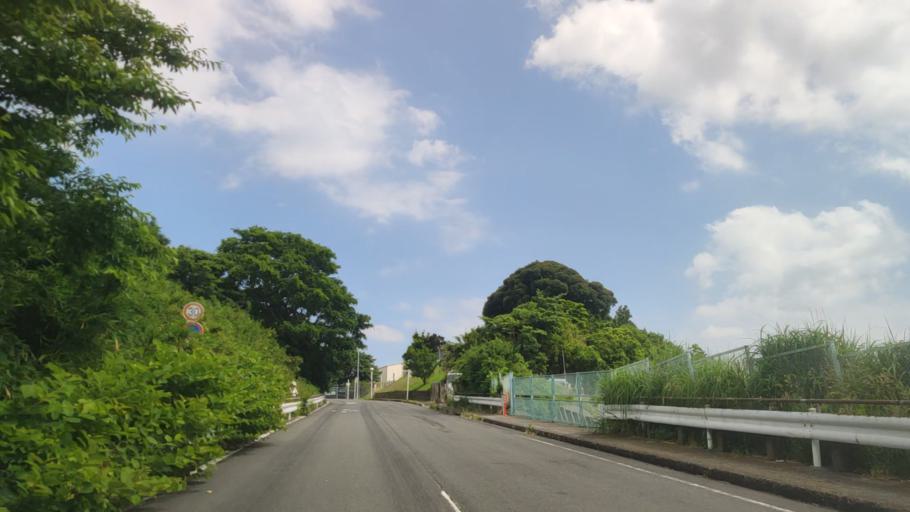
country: JP
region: Kanagawa
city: Yokohama
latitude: 35.4298
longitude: 139.6238
